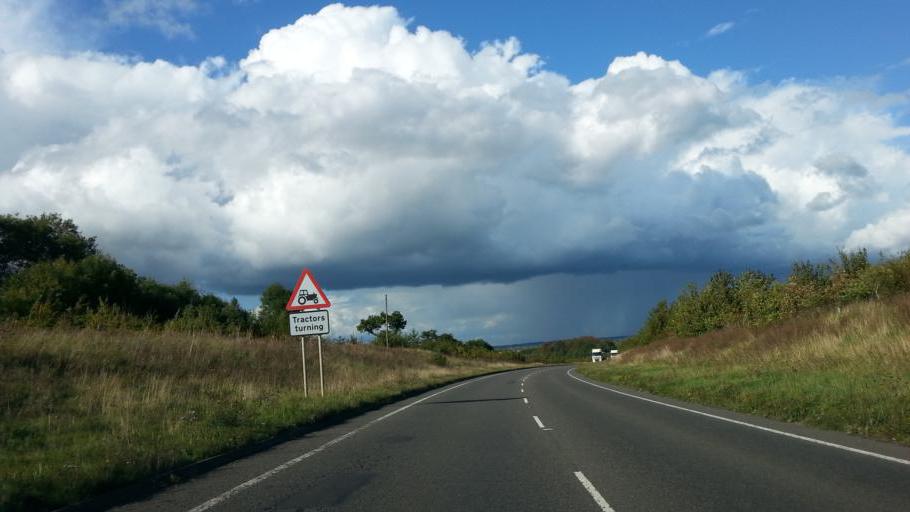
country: GB
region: England
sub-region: Cambridgeshire
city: Papworth Everard
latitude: 52.2471
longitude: -0.1295
